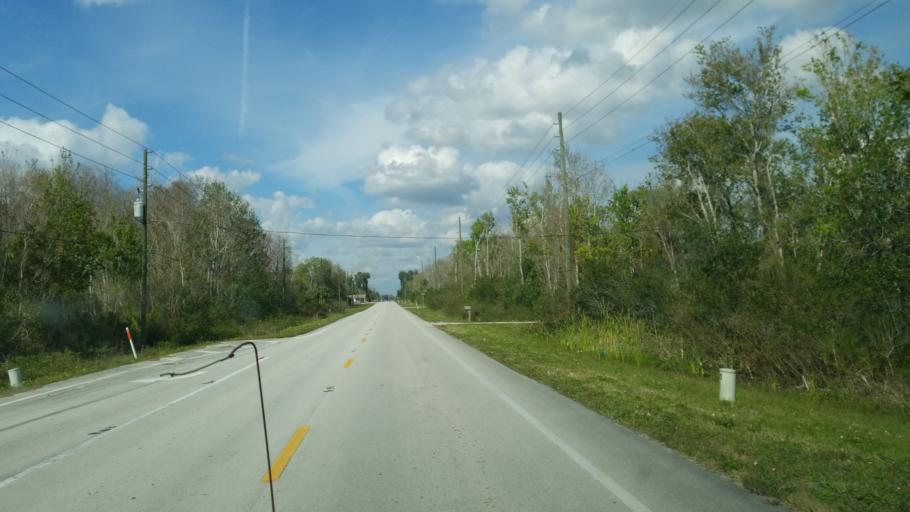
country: US
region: Florida
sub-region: Osceola County
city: Saint Cloud
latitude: 28.1314
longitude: -81.0763
